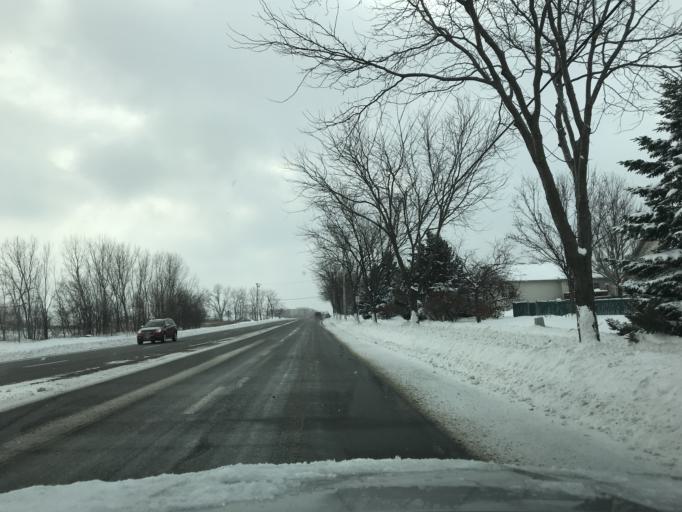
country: US
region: Wisconsin
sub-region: Dane County
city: Sun Prairie
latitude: 43.1632
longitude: -89.2851
